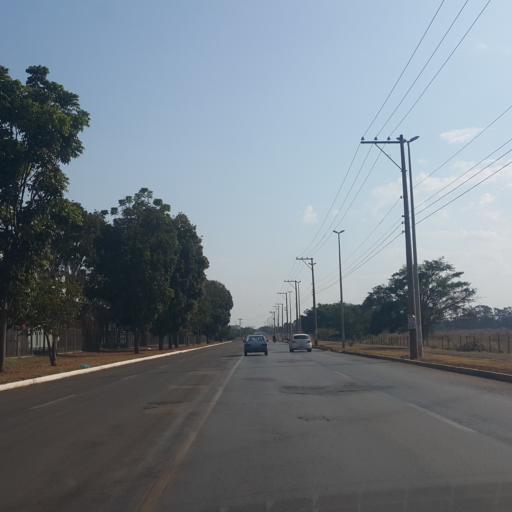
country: BR
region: Federal District
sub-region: Brasilia
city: Brasilia
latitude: -15.8705
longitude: -48.0404
